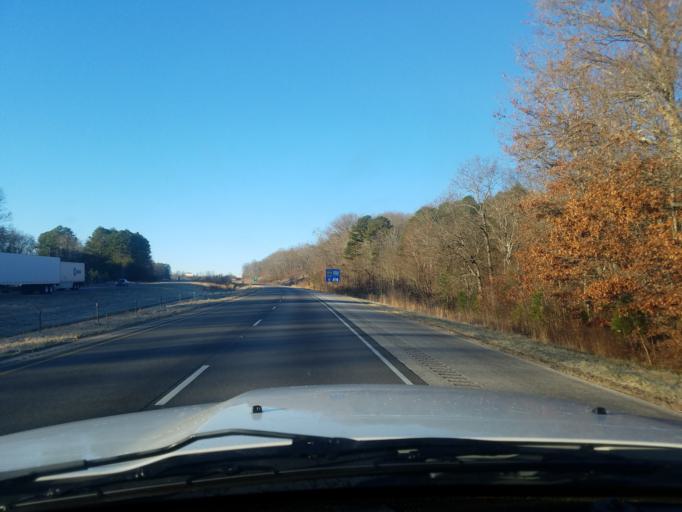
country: US
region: Indiana
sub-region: Crawford County
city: English
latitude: 38.2336
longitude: -86.5623
